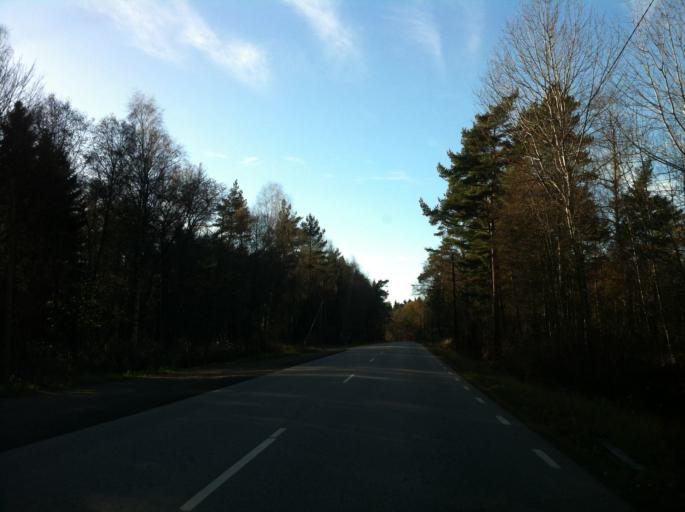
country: SE
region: Blekinge
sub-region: Ronneby Kommun
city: Brakne-Hoby
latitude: 56.2075
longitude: 14.9899
